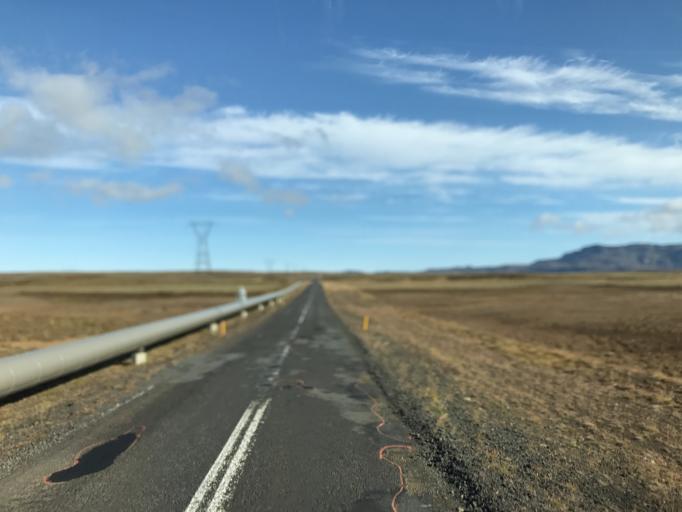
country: IS
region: Capital Region
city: Mosfellsbaer
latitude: 64.1138
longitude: -21.5152
